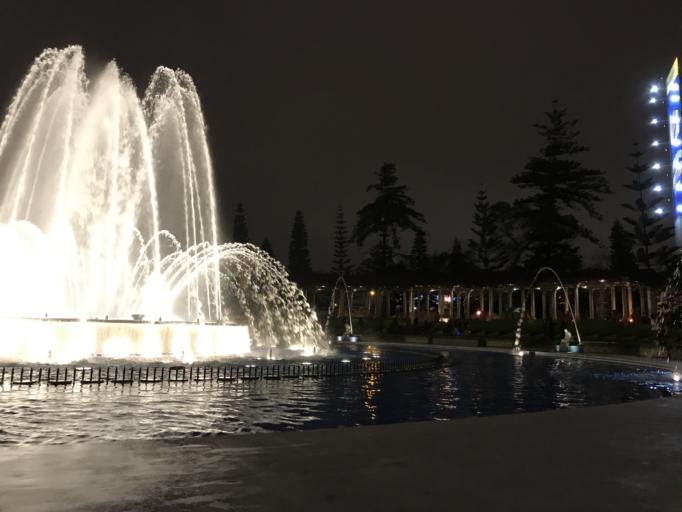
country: PE
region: Lima
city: Lima
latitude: -12.0707
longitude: -77.0331
